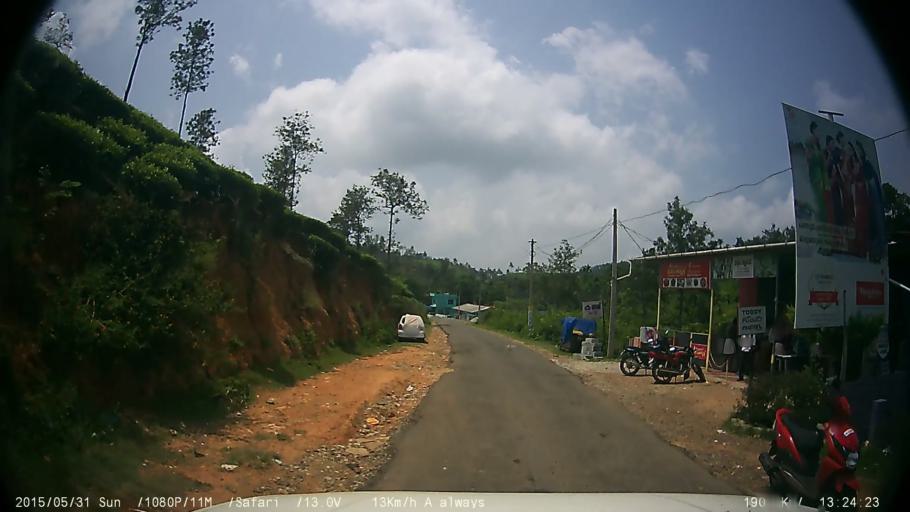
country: IN
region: Kerala
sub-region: Wayanad
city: Kalpetta
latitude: 11.5406
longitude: 76.1383
